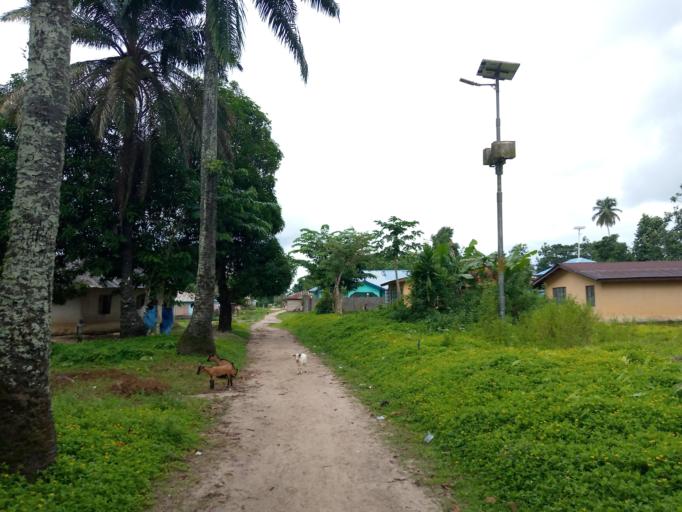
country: SL
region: Southern Province
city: Bonthe
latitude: 7.5303
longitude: -12.5078
